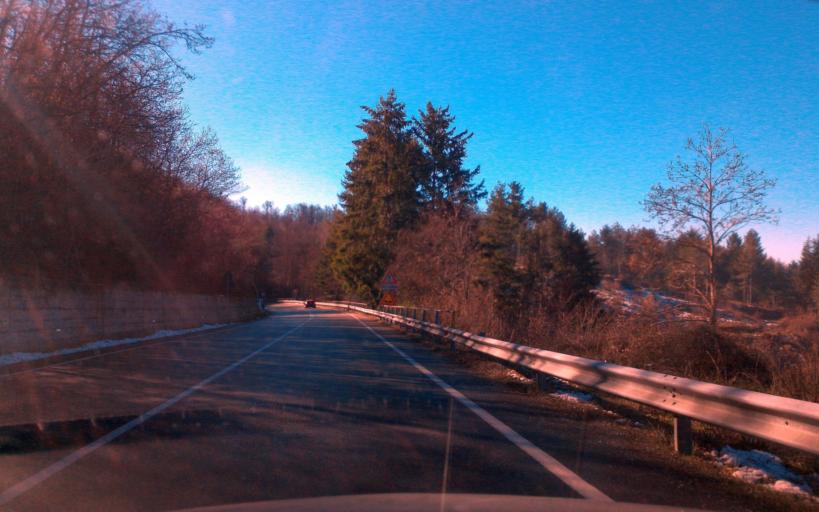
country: IT
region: Calabria
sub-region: Provincia di Cosenza
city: Celico
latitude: 39.3110
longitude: 16.3544
